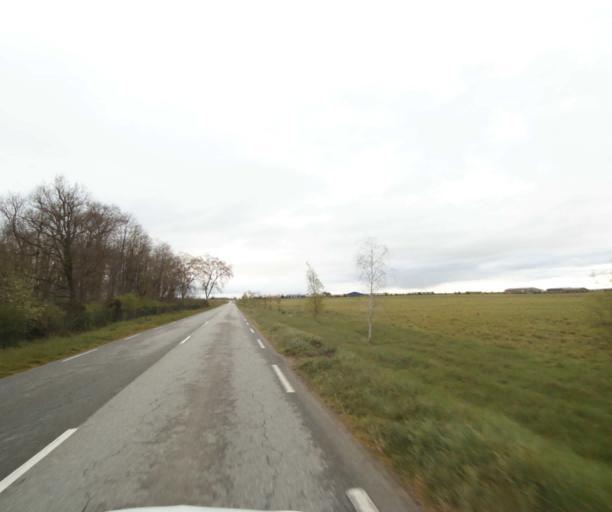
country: FR
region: Midi-Pyrenees
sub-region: Departement de l'Ariege
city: Saverdun
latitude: 43.2320
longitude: 1.6253
